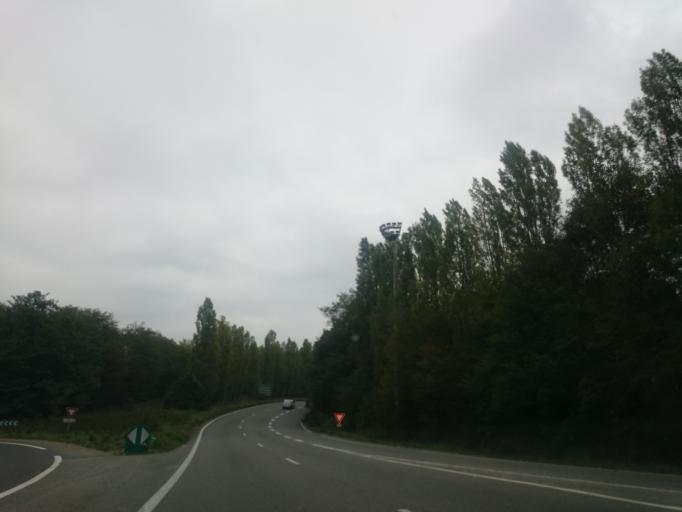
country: FR
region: Ile-de-France
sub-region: Departement de l'Essonne
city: Ris-Orangis
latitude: 48.6339
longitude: 2.4062
